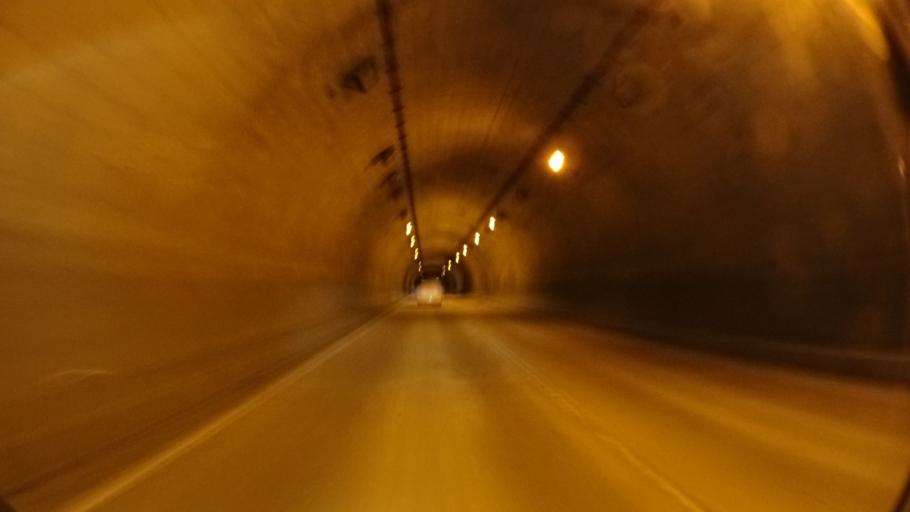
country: JP
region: Hyogo
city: Toyooka
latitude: 35.5043
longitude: 134.8666
